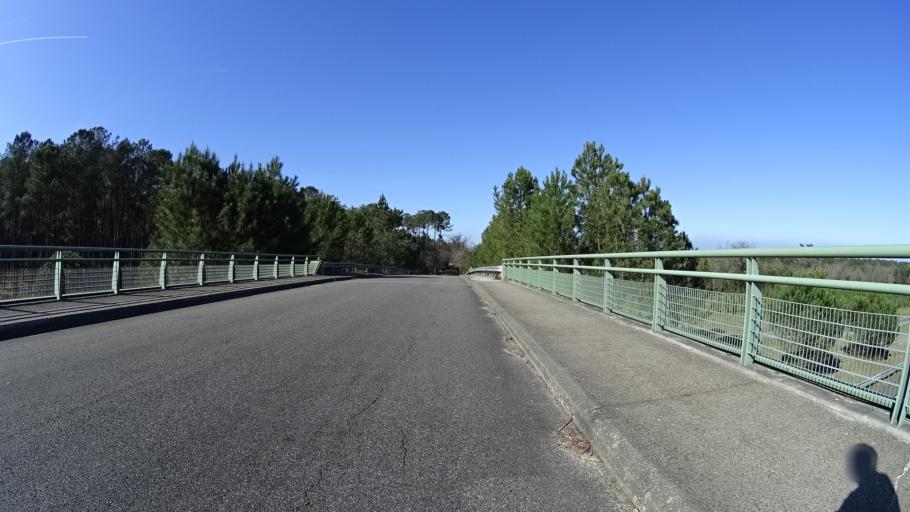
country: FR
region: Aquitaine
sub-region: Departement des Landes
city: Mees
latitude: 43.7383
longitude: -1.0961
